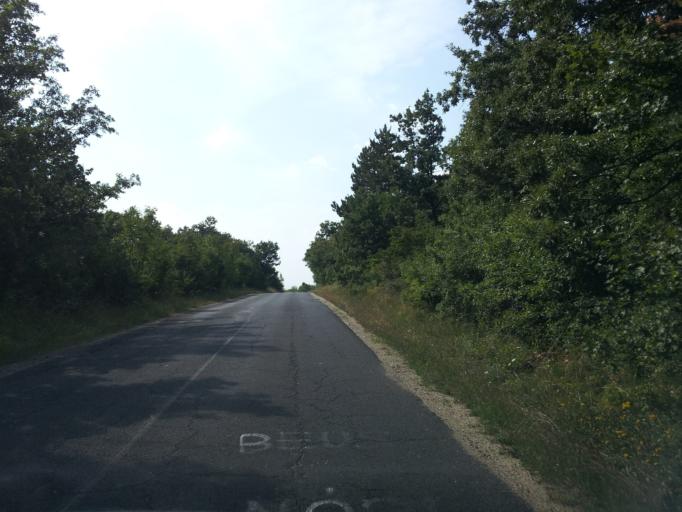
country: HU
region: Veszprem
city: Balatonfured
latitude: 46.9945
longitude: 17.8060
